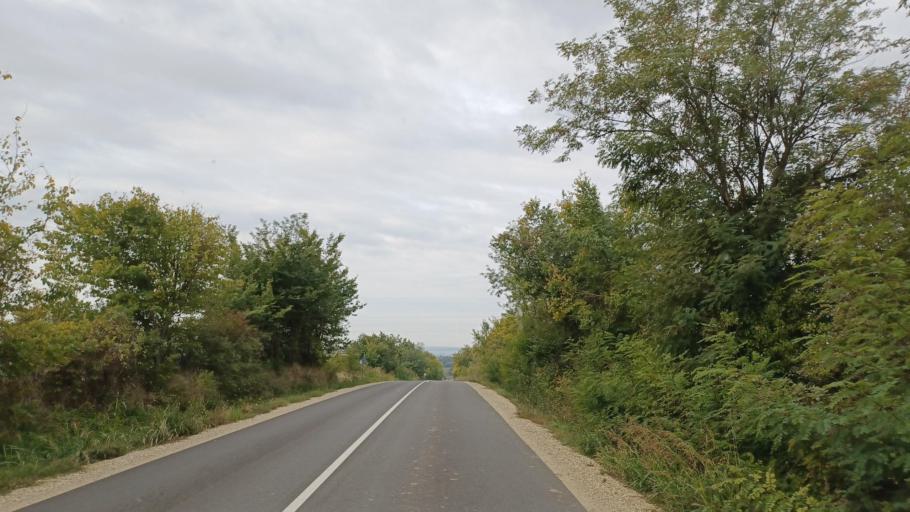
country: HU
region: Tolna
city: Nagydorog
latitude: 46.6064
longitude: 18.7292
